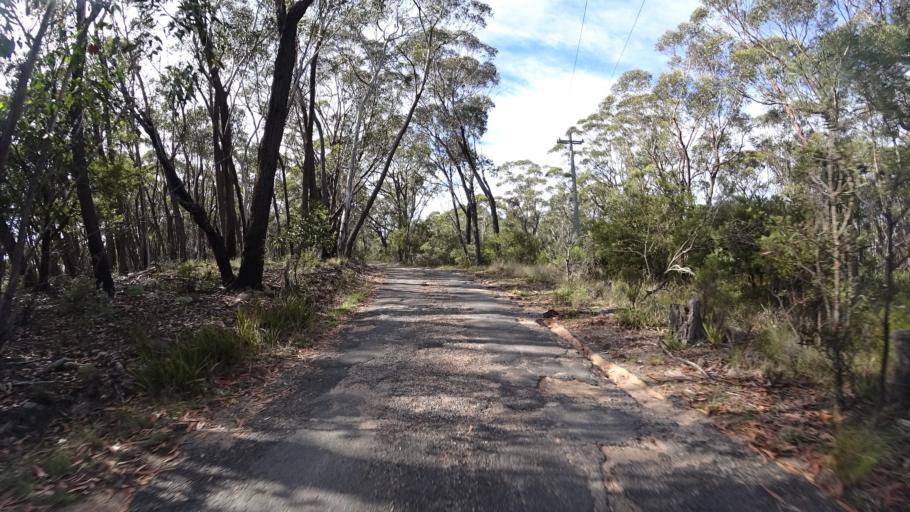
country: AU
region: New South Wales
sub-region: Lithgow
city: Lithgow
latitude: -33.4917
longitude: 150.1642
